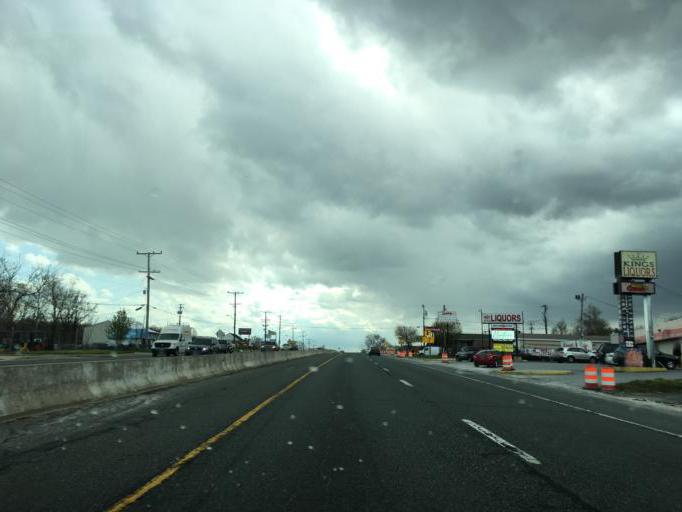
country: US
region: Maryland
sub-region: Baltimore County
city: Rosedale
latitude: 39.3228
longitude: -76.5035
